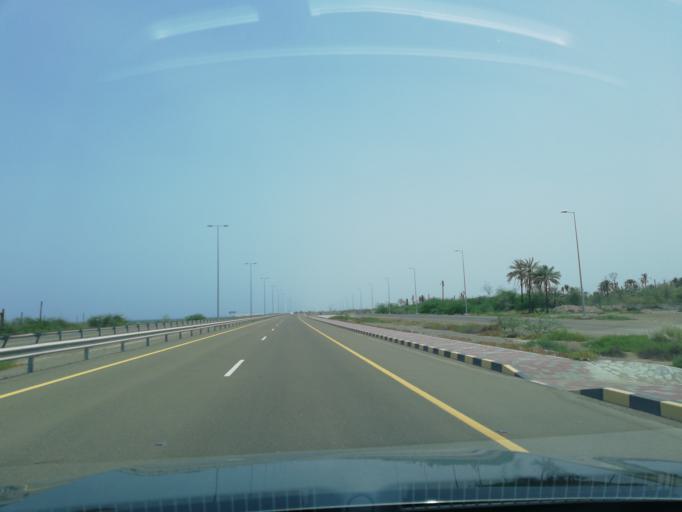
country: OM
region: Al Batinah
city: Al Liwa'
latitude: 24.6326
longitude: 56.5262
